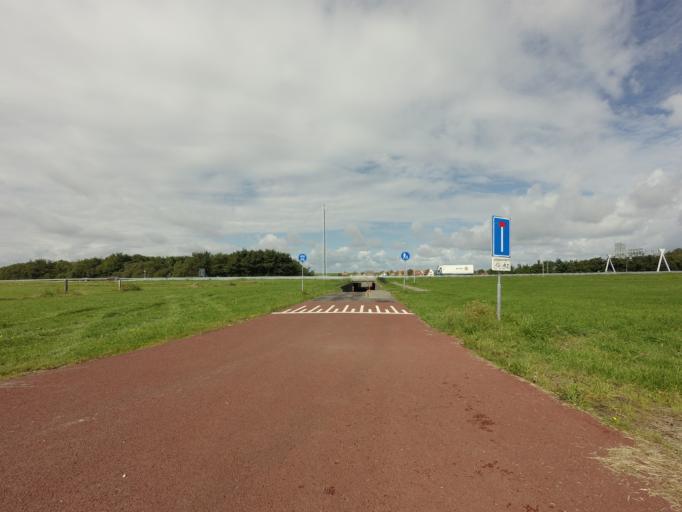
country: NL
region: Friesland
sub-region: Sudwest Fryslan
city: Makkum
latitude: 53.1077
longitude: 5.3937
